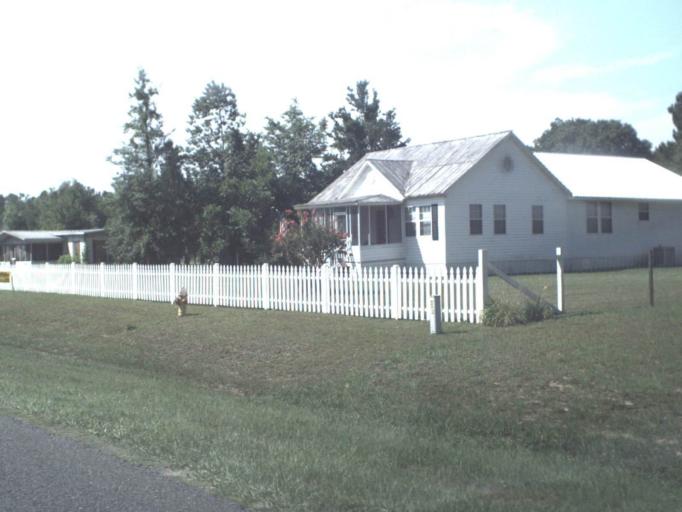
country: US
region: Florida
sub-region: Nassau County
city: Hilliard
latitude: 30.7017
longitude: -81.9253
